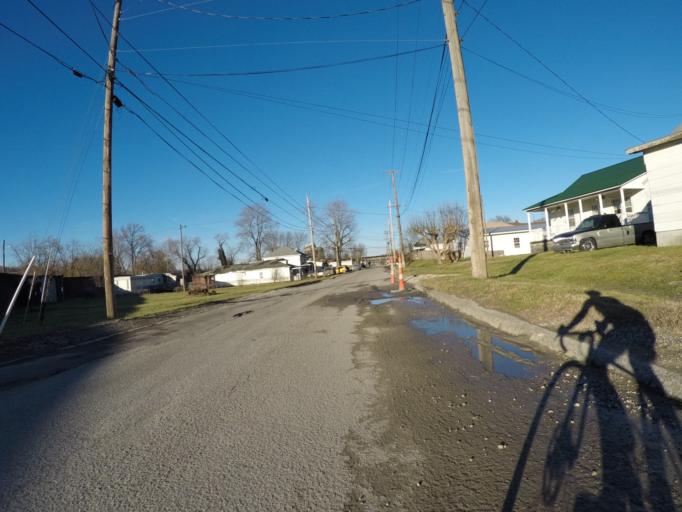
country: US
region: Kentucky
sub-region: Boyd County
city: Catlettsburg
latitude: 38.4003
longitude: -82.5925
